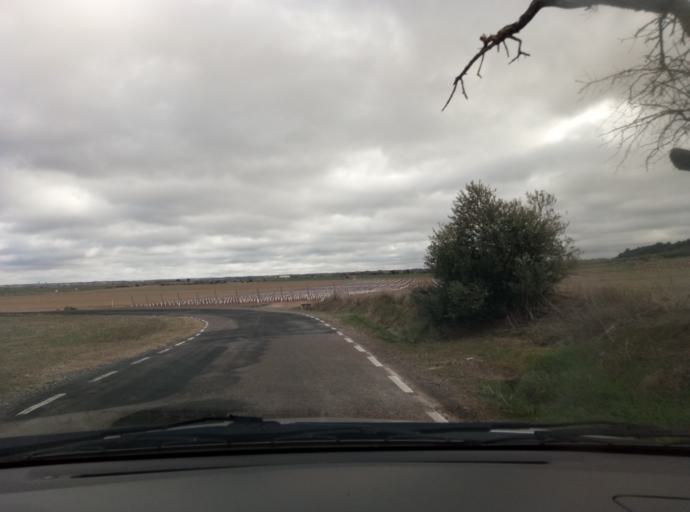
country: ES
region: Catalonia
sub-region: Provincia de Lleida
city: Nalec
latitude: 41.5932
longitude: 1.0888
